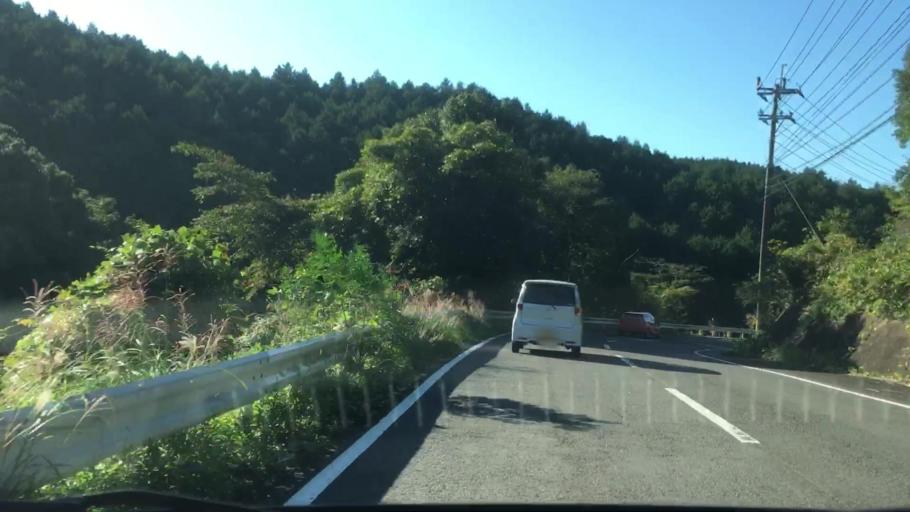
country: JP
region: Nagasaki
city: Sasebo
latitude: 32.9639
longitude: 129.6877
